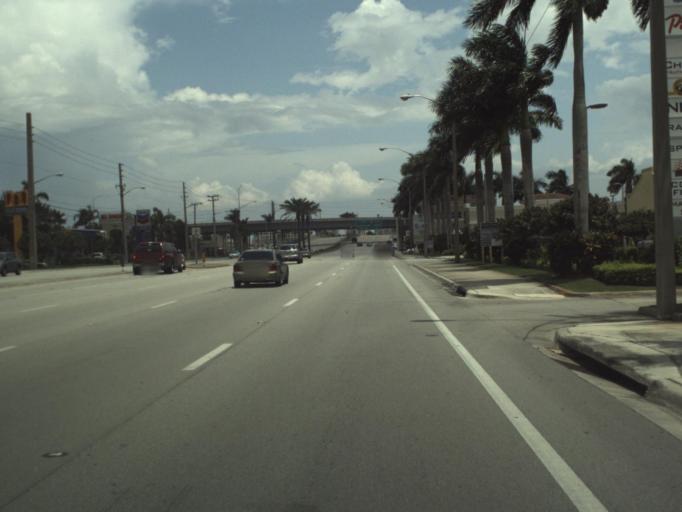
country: US
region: Florida
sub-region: Palm Beach County
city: West Palm Beach
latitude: 26.7061
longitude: -80.0813
